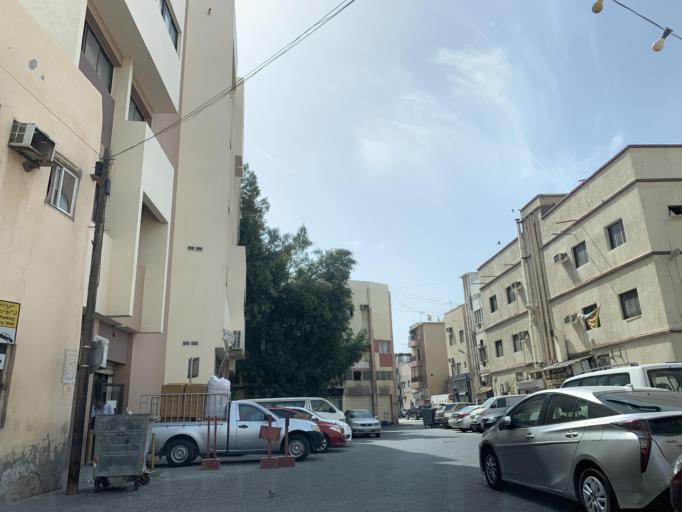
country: BH
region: Manama
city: Manama
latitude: 26.2336
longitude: 50.5787
